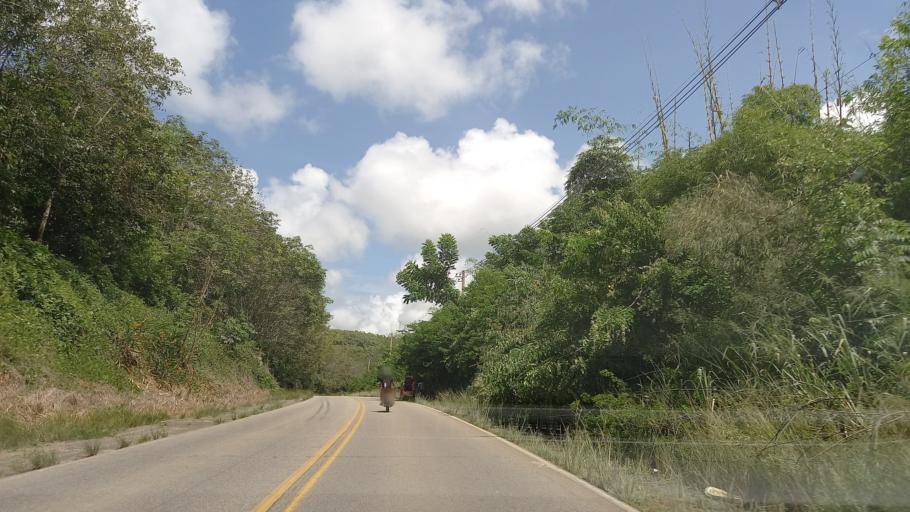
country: BR
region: Pernambuco
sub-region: Rio Formoso
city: Rio Formoso
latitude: -8.6436
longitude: -35.1197
